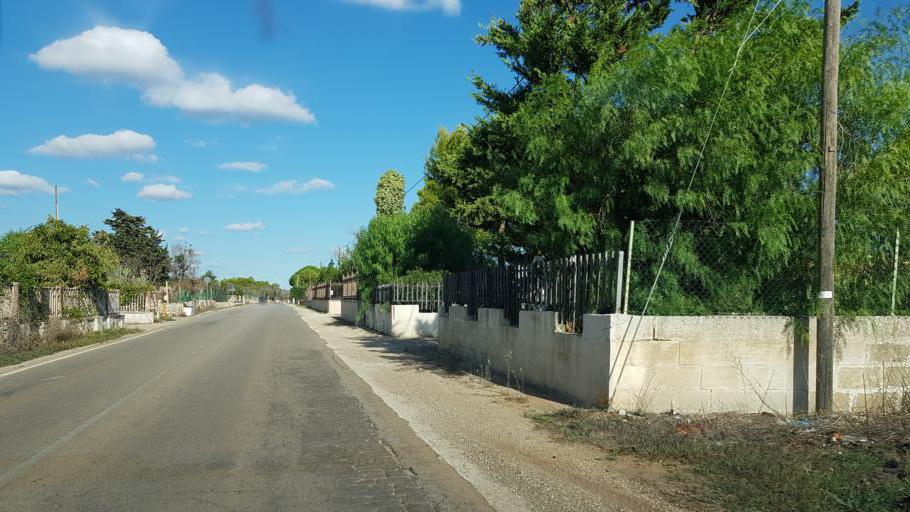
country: IT
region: Apulia
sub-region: Provincia di Lecce
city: Nardo
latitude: 40.1308
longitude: 18.0347
